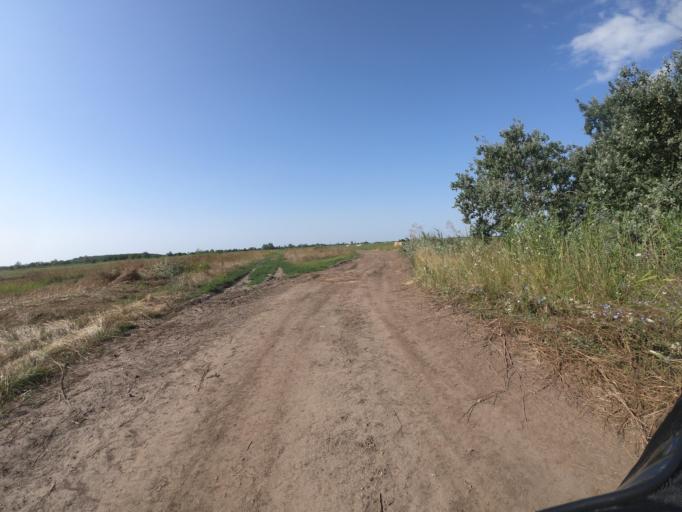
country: HU
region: Hajdu-Bihar
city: Egyek
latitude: 47.5944
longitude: 20.9681
